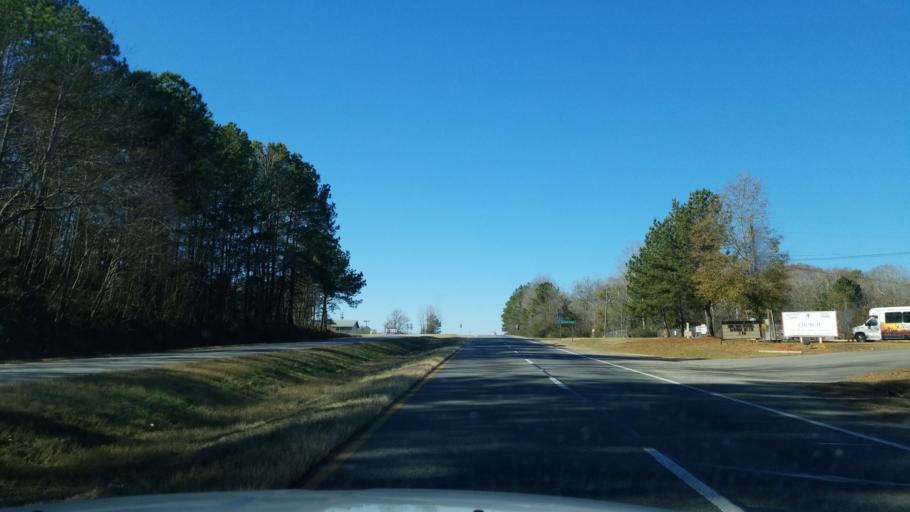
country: US
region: Alabama
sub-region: Tuscaloosa County
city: Northport
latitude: 33.2507
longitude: -87.6839
